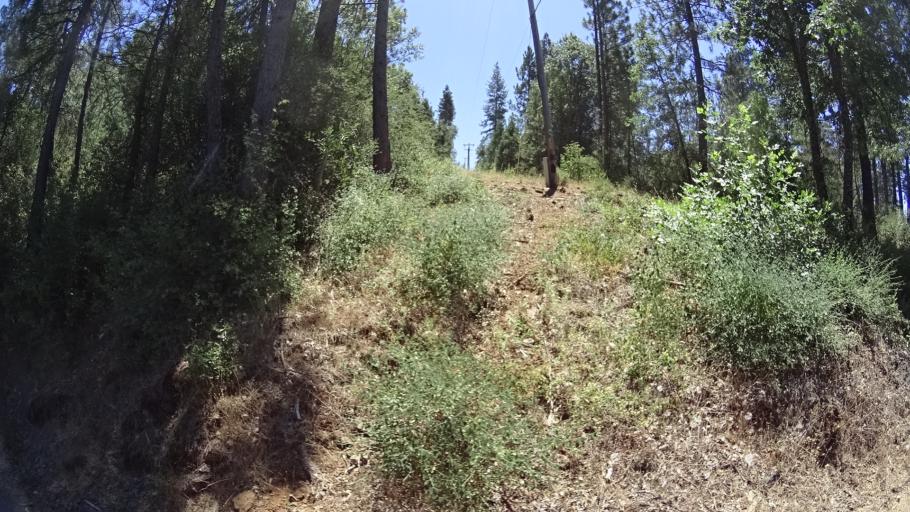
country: US
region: California
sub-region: Calaveras County
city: Mountain Ranch
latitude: 38.2710
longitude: -120.4944
